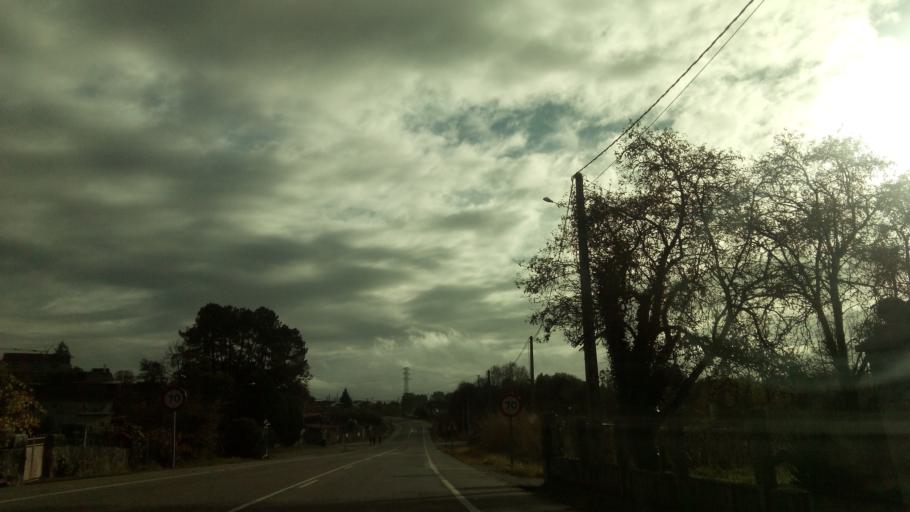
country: ES
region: Galicia
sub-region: Provincia de Pontevedra
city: Ponteareas
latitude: 42.1920
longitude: -8.5084
